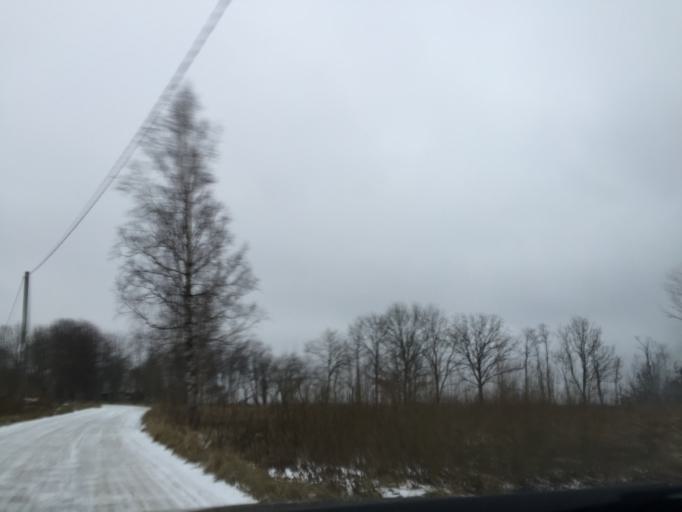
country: LV
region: Salacgrivas
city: Salacgriva
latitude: 57.5094
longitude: 24.3820
